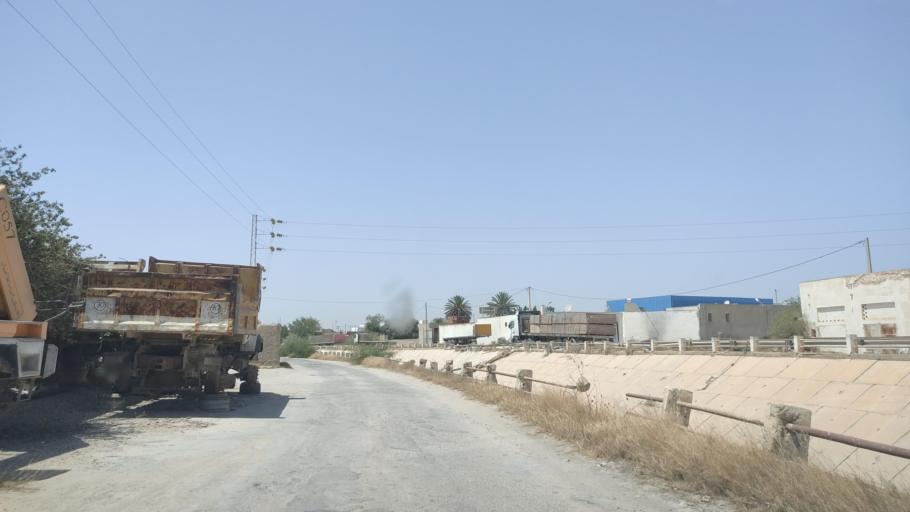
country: TN
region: Safaqis
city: Sfax
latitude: 34.7139
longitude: 10.7318
